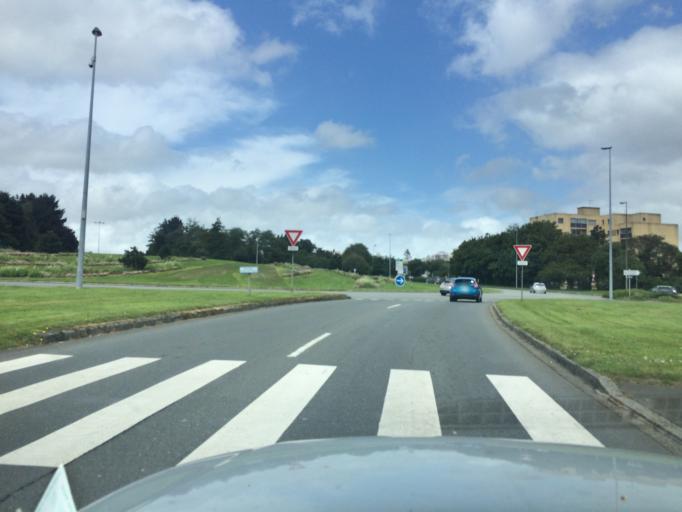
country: FR
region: Brittany
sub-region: Departement du Finistere
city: Brest
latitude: 48.4137
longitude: -4.4799
